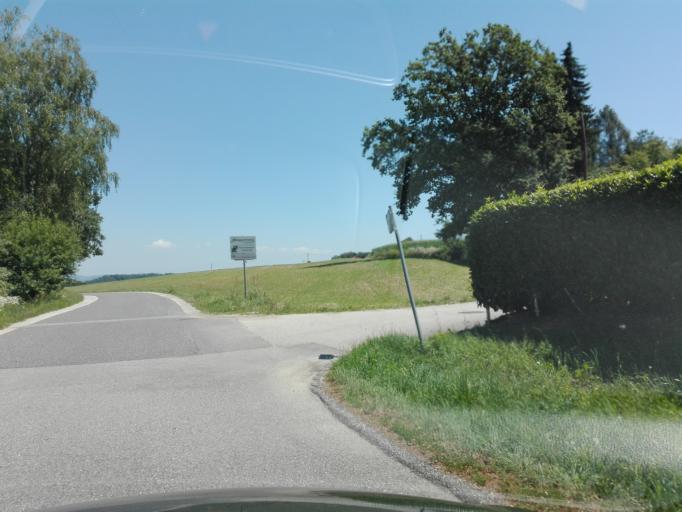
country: AT
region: Upper Austria
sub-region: Politischer Bezirk Urfahr-Umgebung
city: Steyregg
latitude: 48.3264
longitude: 14.3741
